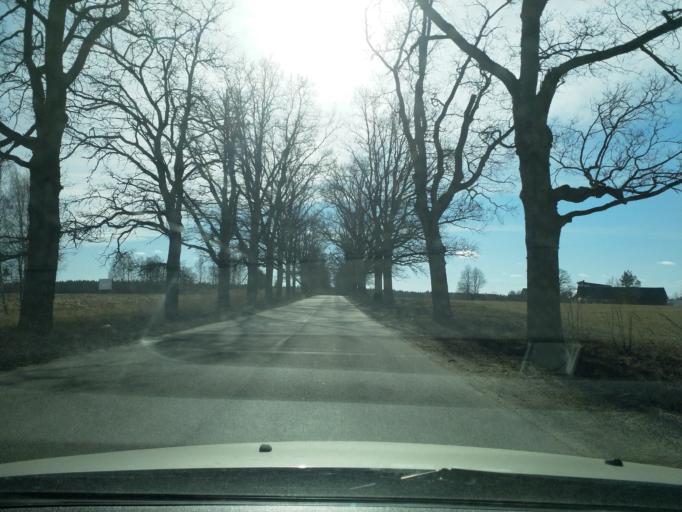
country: LV
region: Valmieras Rajons
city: Valmiera
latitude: 57.5177
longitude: 25.4203
